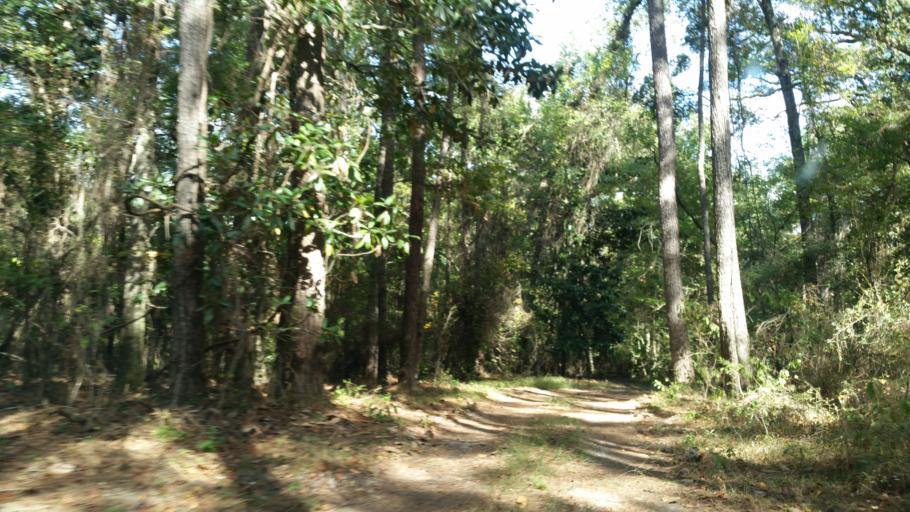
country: US
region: Alabama
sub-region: Baldwin County
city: Spanish Fort
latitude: 30.7377
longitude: -87.9232
